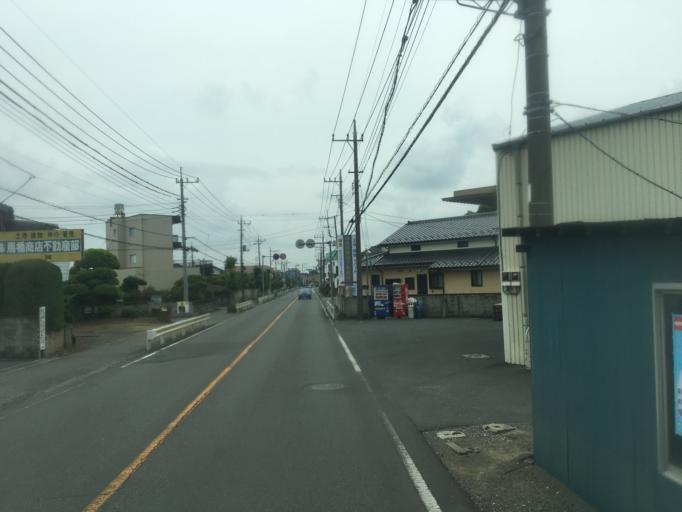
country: JP
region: Saitama
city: Sakado
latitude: 35.9872
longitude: 139.4484
